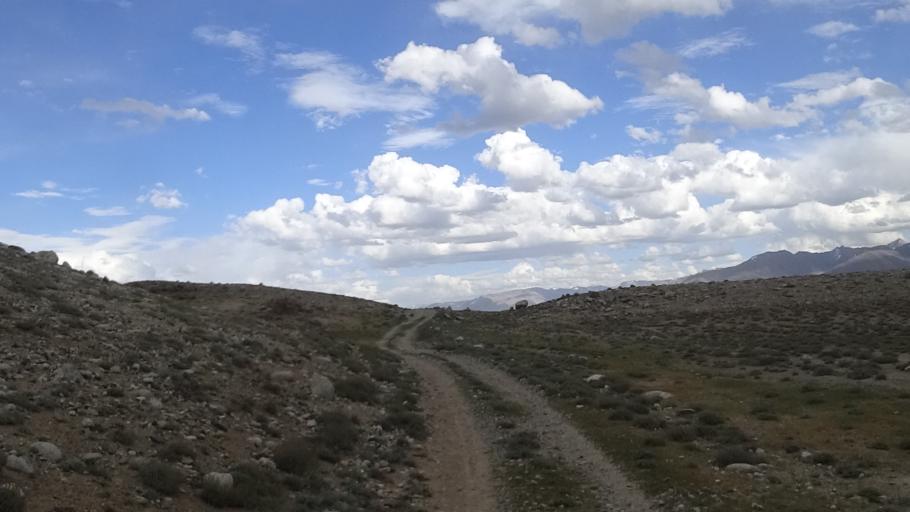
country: TJ
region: Gorno-Badakhshan
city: Murghob
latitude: 37.4688
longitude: 73.6027
